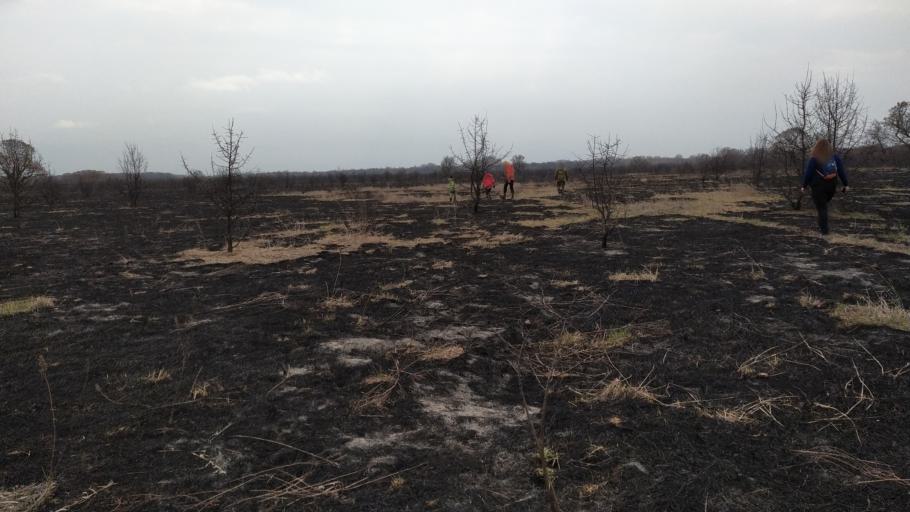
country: RU
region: Rostov
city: Semikarakorsk
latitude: 47.5500
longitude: 40.6779
